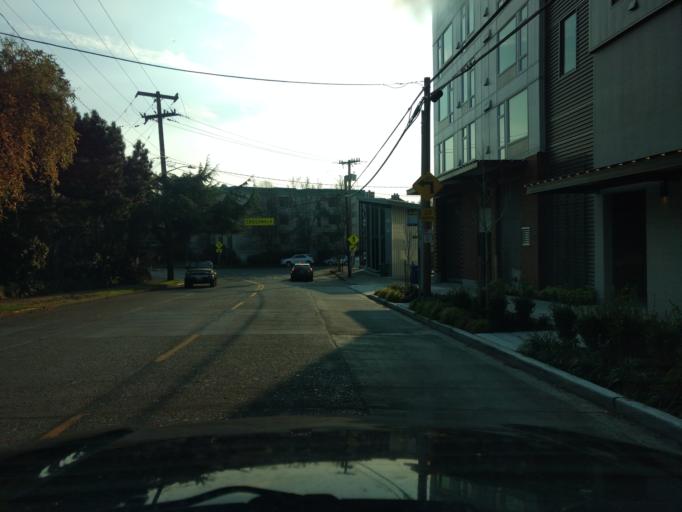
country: US
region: Washington
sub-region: King County
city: Seattle
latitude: 47.6800
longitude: -122.3229
